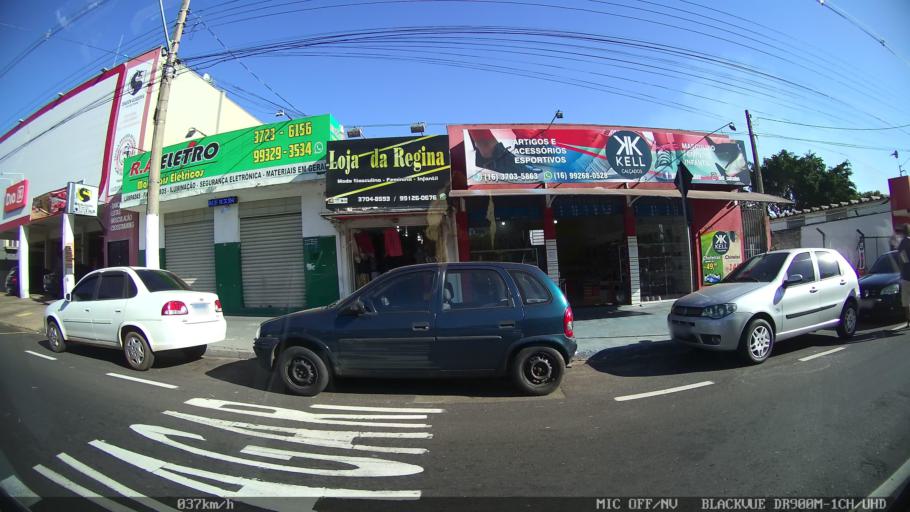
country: BR
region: Sao Paulo
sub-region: Franca
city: Franca
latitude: -20.4976
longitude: -47.4195
